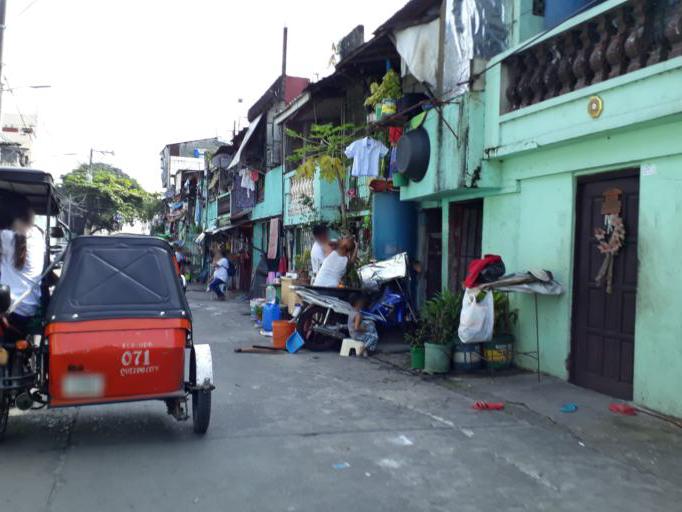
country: PH
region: Calabarzon
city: Bagong Pagasa
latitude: 14.6719
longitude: 121.0012
